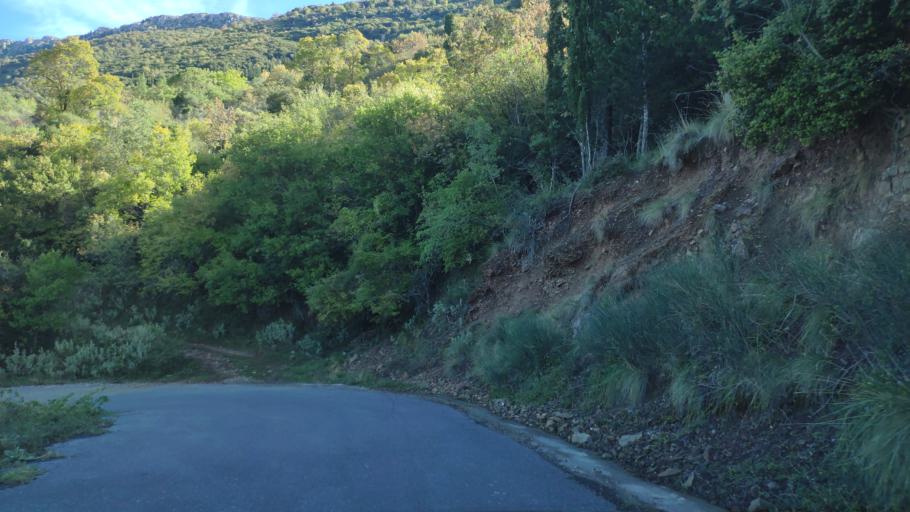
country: GR
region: Peloponnese
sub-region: Nomos Arkadias
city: Dimitsana
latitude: 37.5519
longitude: 22.0565
